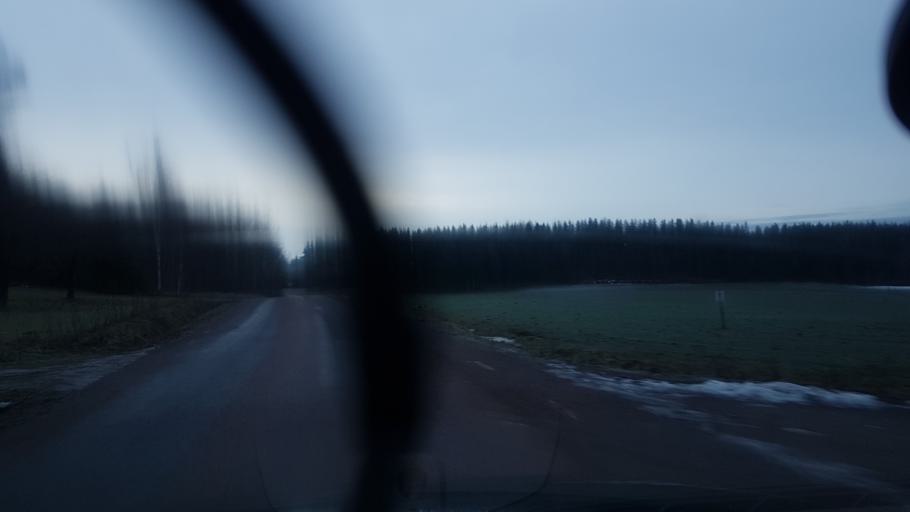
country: SE
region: Dalarna
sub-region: Borlange Kommun
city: Ornas
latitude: 60.4405
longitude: 15.6466
